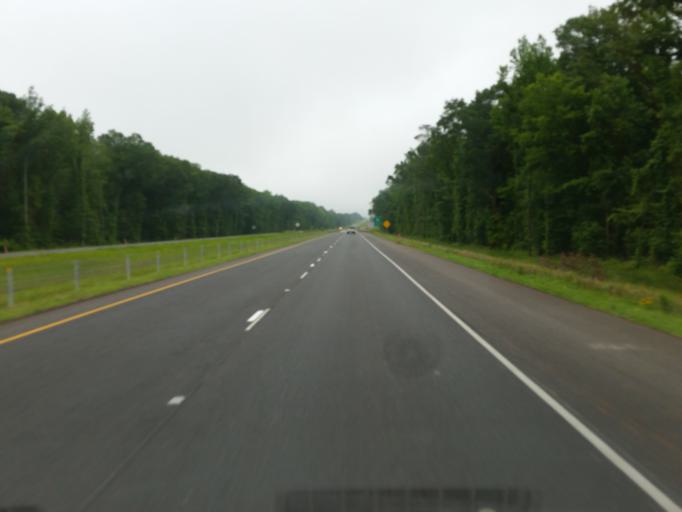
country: US
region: Louisiana
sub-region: Bienville Parish
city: Arcadia
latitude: 32.5631
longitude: -93.0941
